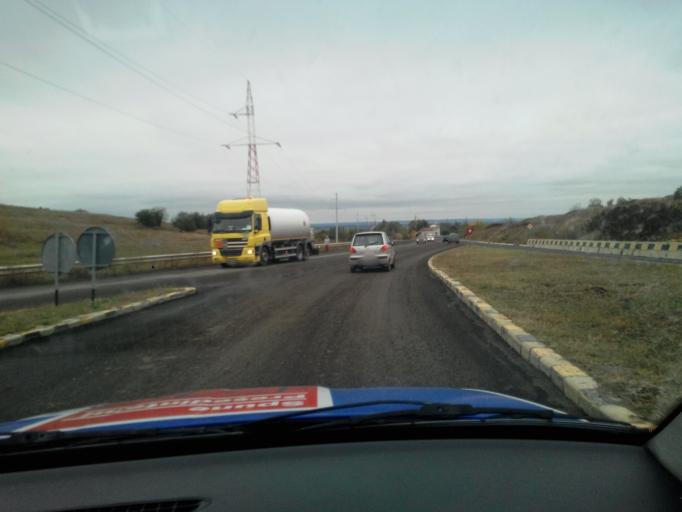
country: RO
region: Giurgiu
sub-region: Comuna Daia
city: Daia
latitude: 43.9991
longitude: 25.9904
